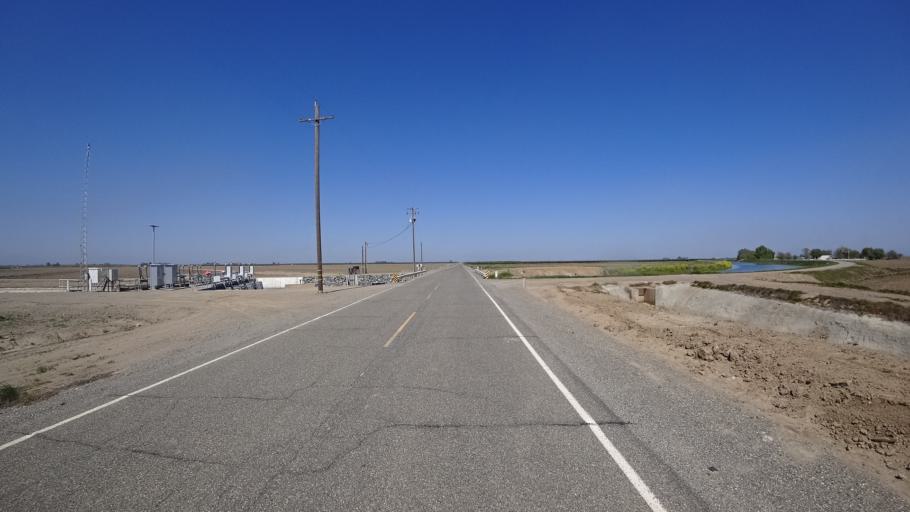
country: US
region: California
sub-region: Glenn County
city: Willows
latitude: 39.5563
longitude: -122.1368
